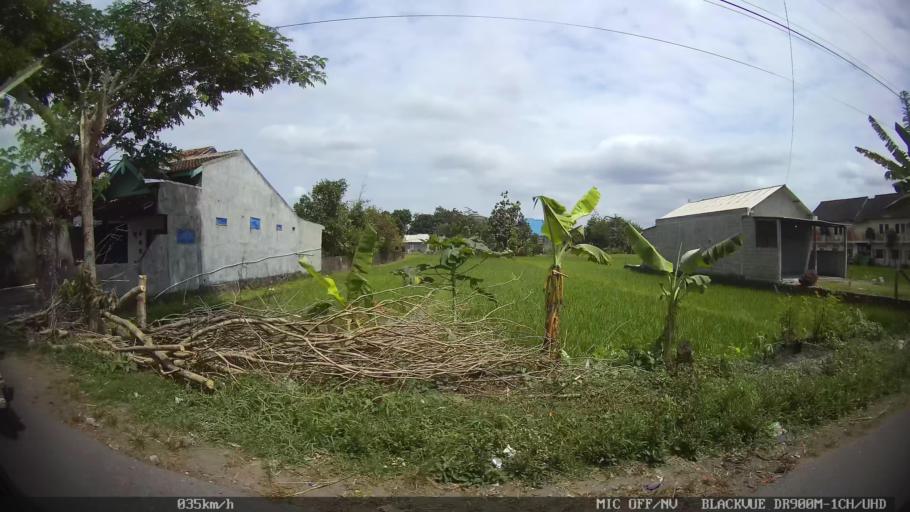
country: ID
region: Daerah Istimewa Yogyakarta
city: Depok
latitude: -7.7931
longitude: 110.4584
